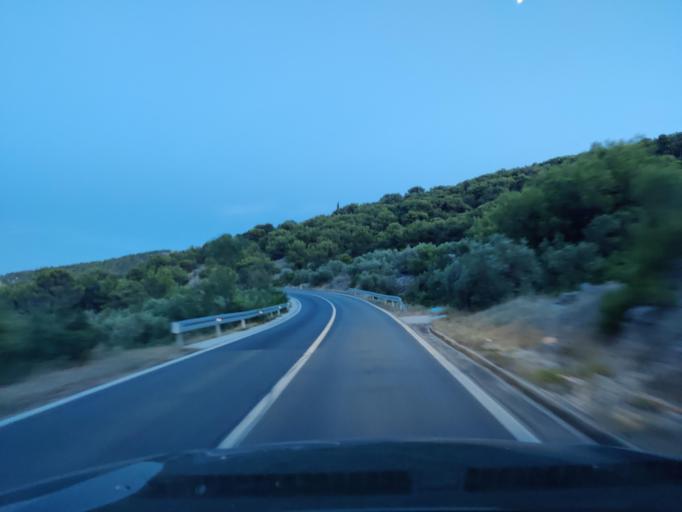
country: HR
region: Sibensko-Kniniska
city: Murter
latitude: 43.8083
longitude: 15.6049
